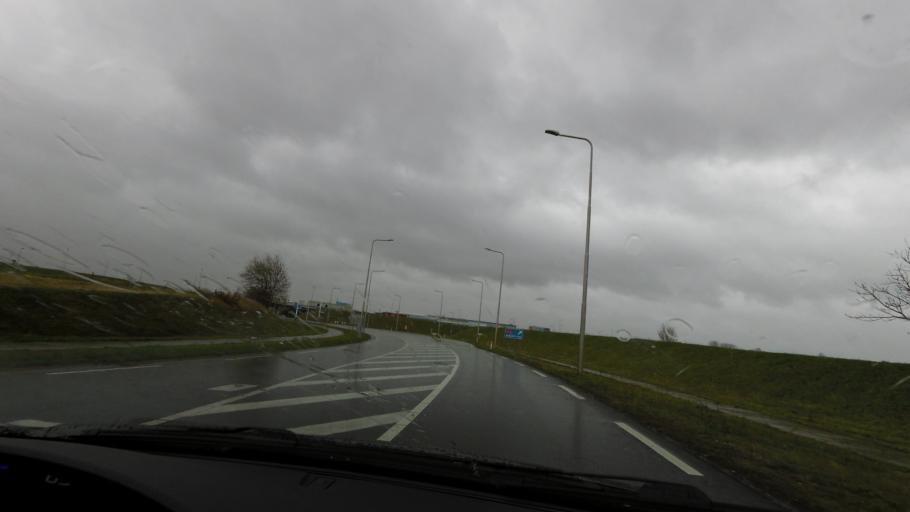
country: NL
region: Limburg
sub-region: Gemeente Stein
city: Elsloo
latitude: 50.9271
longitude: 5.7725
